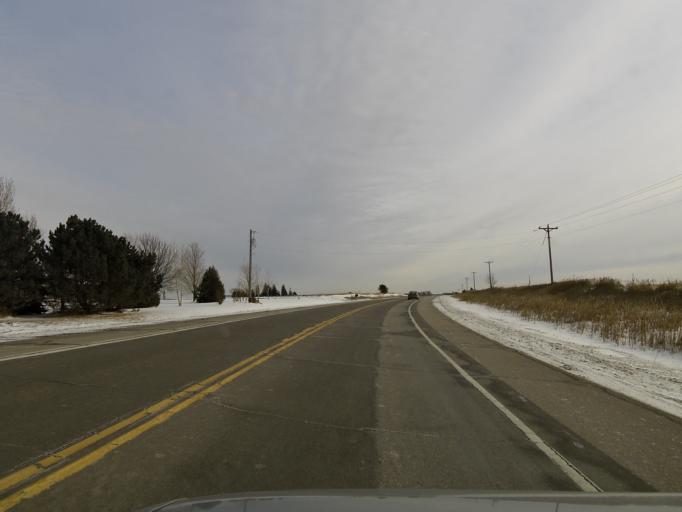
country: US
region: Minnesota
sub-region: Scott County
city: Jordan
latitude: 44.6814
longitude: -93.5685
